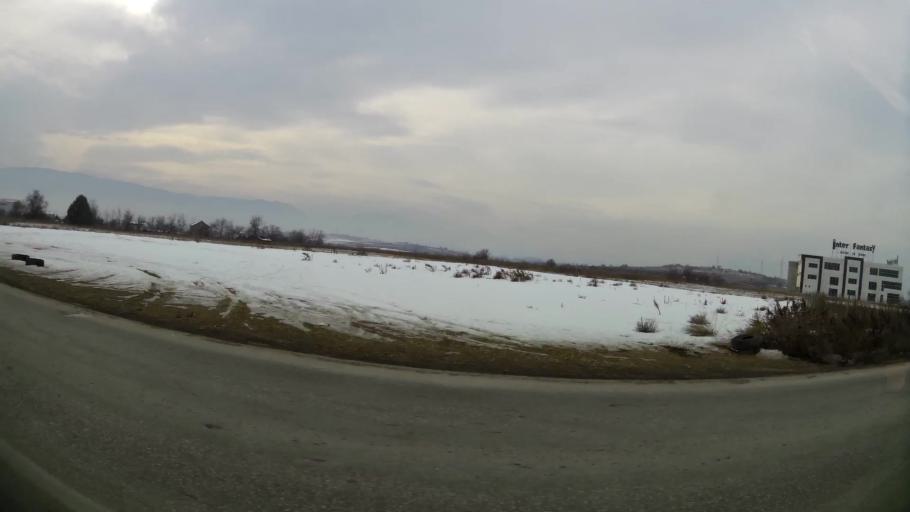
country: MK
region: Suto Orizari
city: Suto Orizare
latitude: 42.0456
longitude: 21.3878
